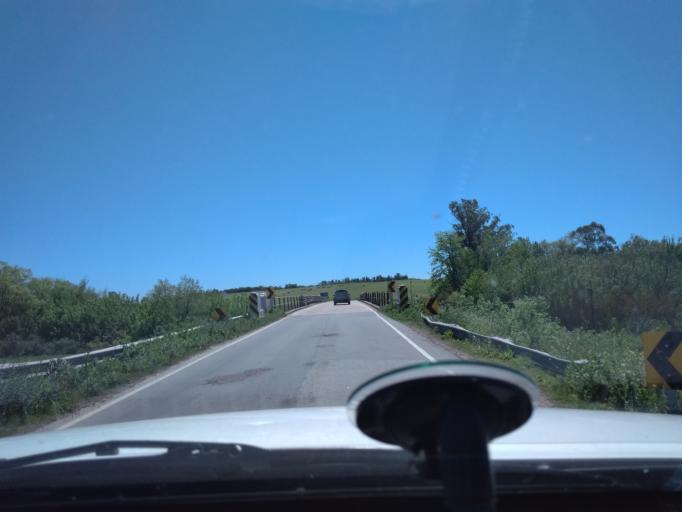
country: UY
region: Canelones
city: Las Piedras
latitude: -34.7194
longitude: -56.2906
